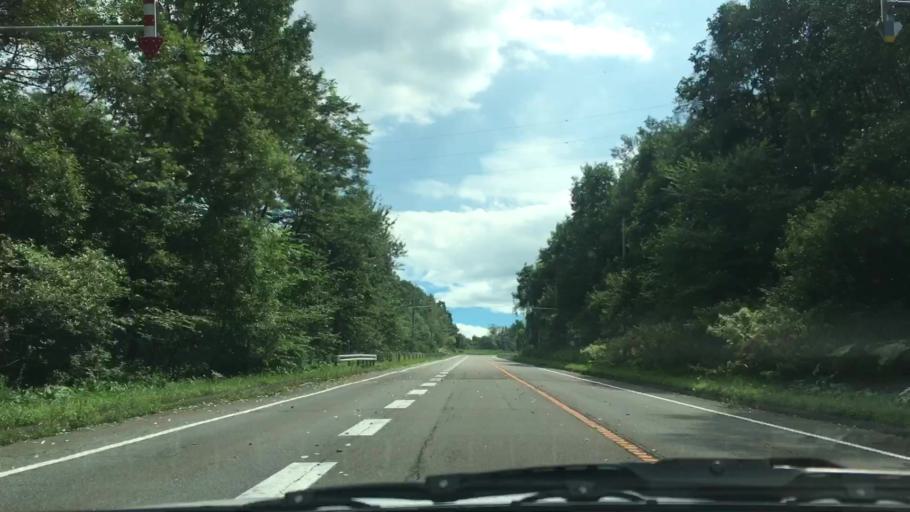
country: JP
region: Hokkaido
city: Otofuke
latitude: 43.2807
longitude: 143.4064
